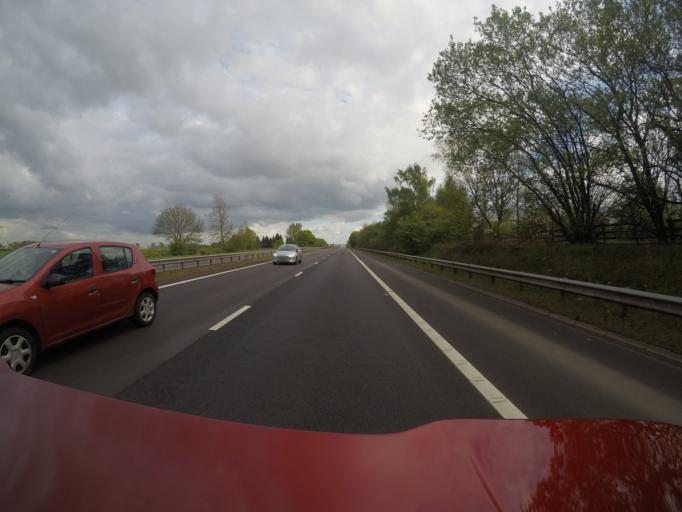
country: GB
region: Scotland
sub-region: Renfrewshire
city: Erskine
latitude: 55.8774
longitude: -4.4742
